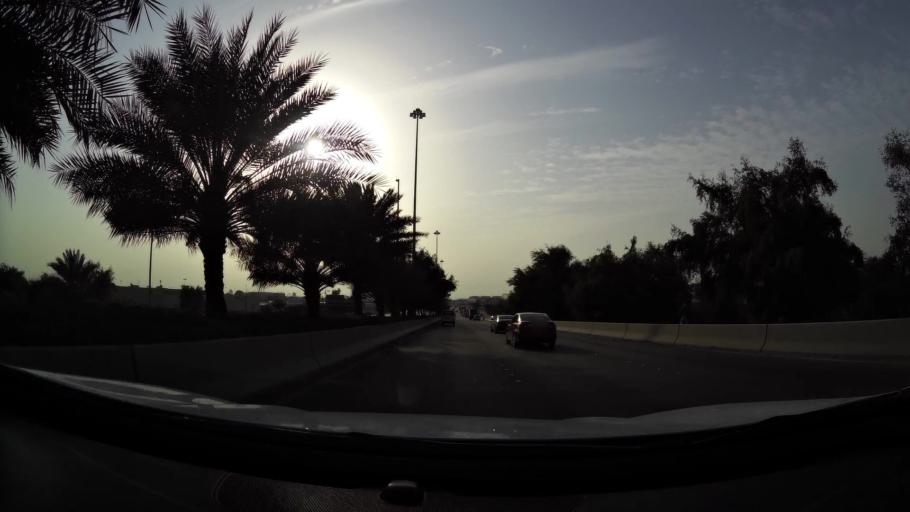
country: AE
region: Abu Dhabi
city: Abu Dhabi
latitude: 24.3468
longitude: 54.5242
